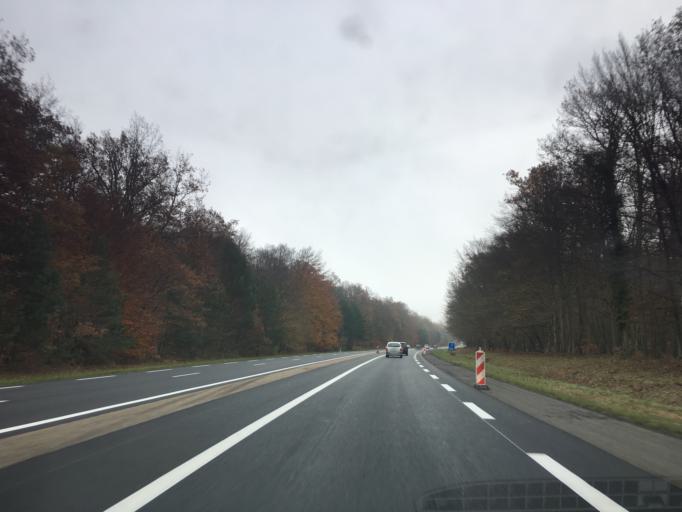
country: FR
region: Ile-de-France
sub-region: Departement de Seine-et-Marne
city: Avon
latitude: 48.3947
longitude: 2.7443
